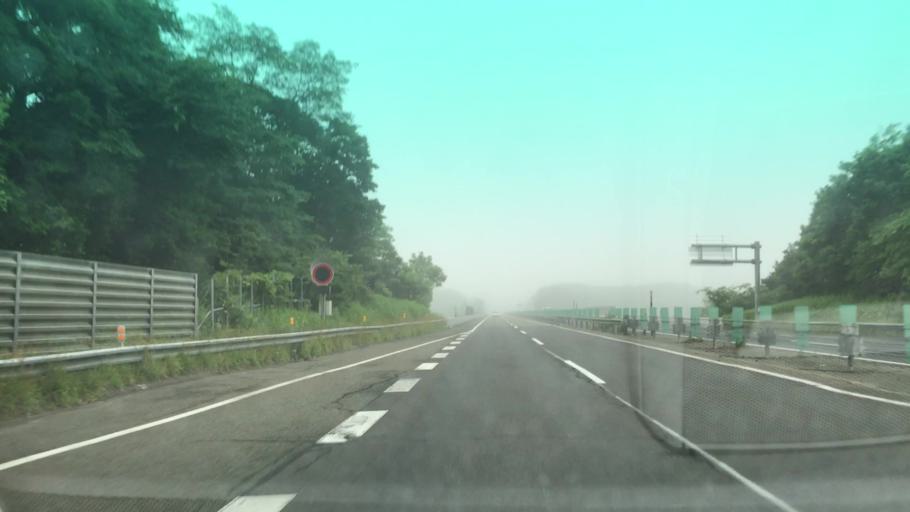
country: JP
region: Hokkaido
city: Chitose
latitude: 42.8087
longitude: 141.6224
